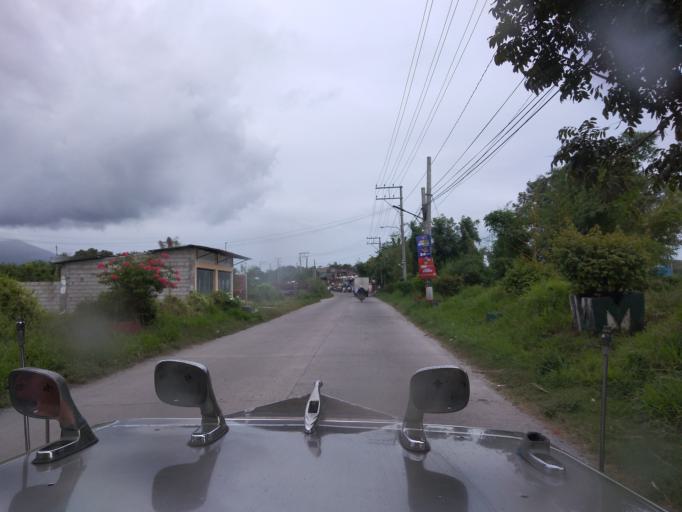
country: PH
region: Central Luzon
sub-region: Province of Pampanga
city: Pandacaqui
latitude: 15.1856
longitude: 120.6408
